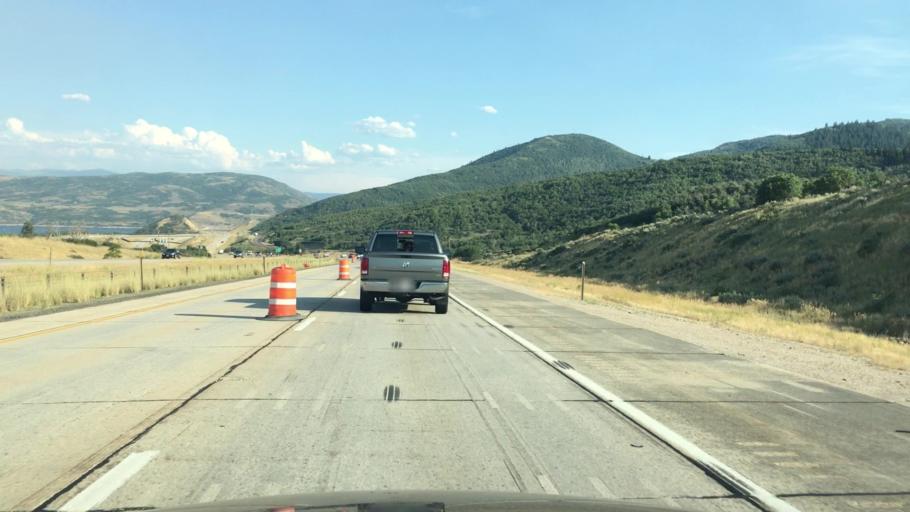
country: US
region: Utah
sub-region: Summit County
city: Park City
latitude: 40.6350
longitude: -111.4499
